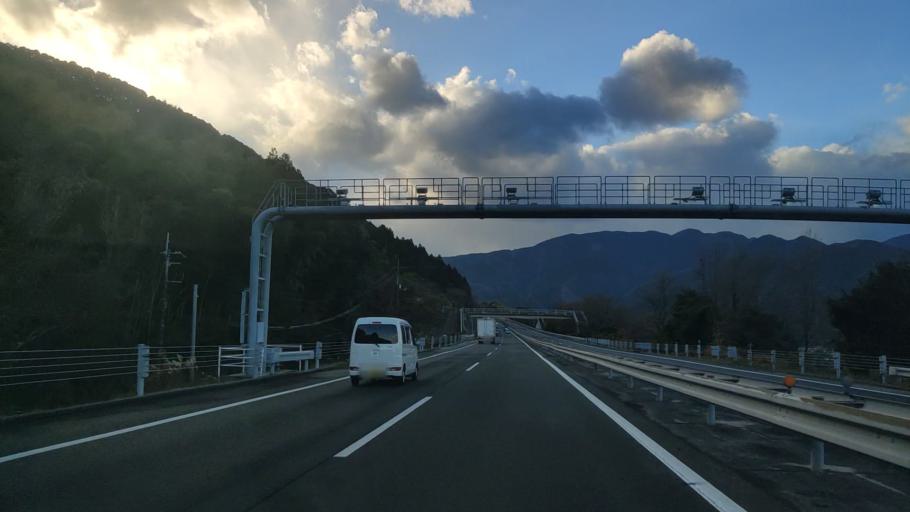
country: JP
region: Ehime
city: Saijo
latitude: 33.8560
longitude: 133.0331
